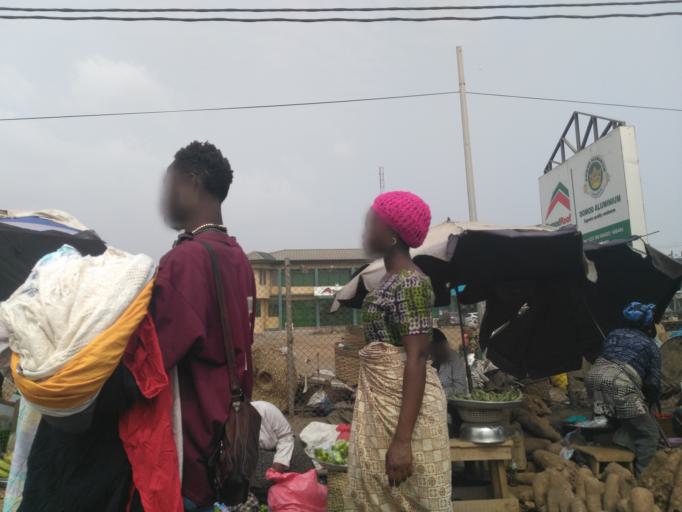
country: GH
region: Greater Accra
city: Accra
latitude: 5.5489
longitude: -0.2190
